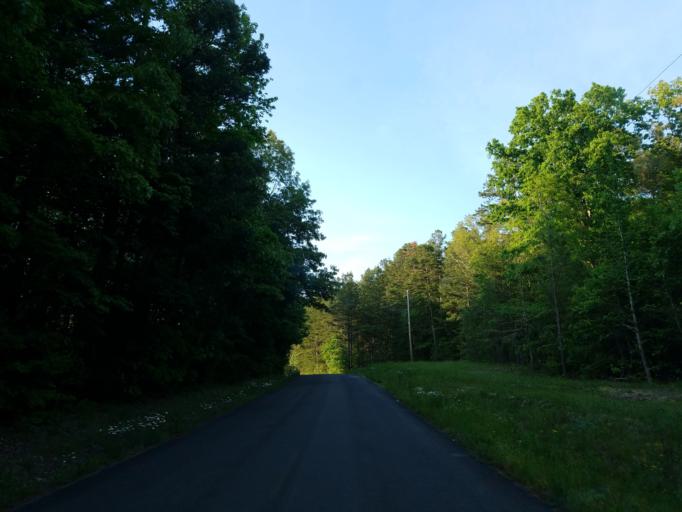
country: US
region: Georgia
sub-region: Whitfield County
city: Dalton
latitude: 34.6537
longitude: -85.0824
